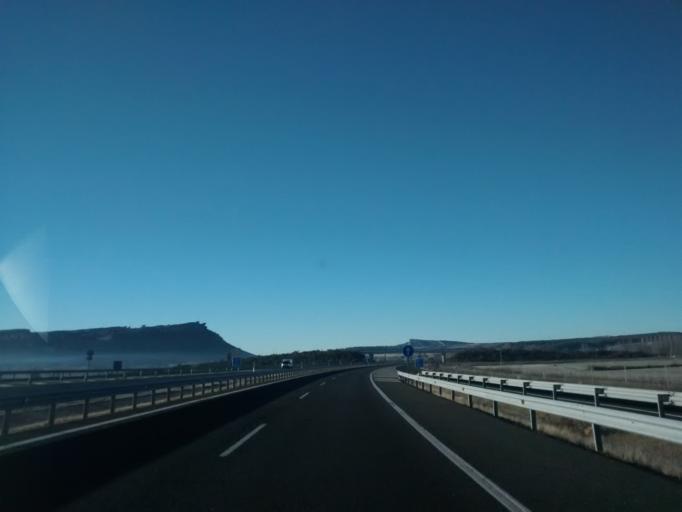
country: ES
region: Castille and Leon
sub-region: Provincia de Palencia
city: Aguilar de Campoo
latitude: 42.7770
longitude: -4.2442
